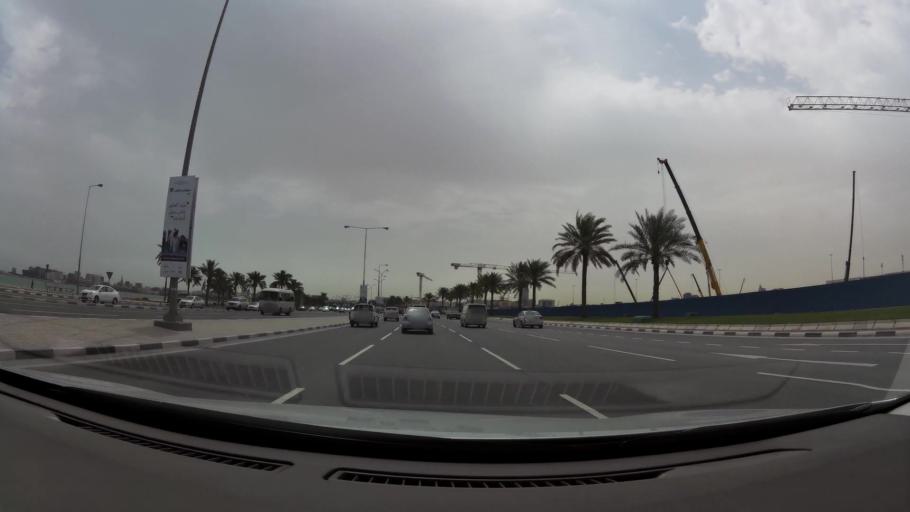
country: QA
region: Baladiyat ad Dawhah
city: Doha
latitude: 25.3026
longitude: 51.5180
